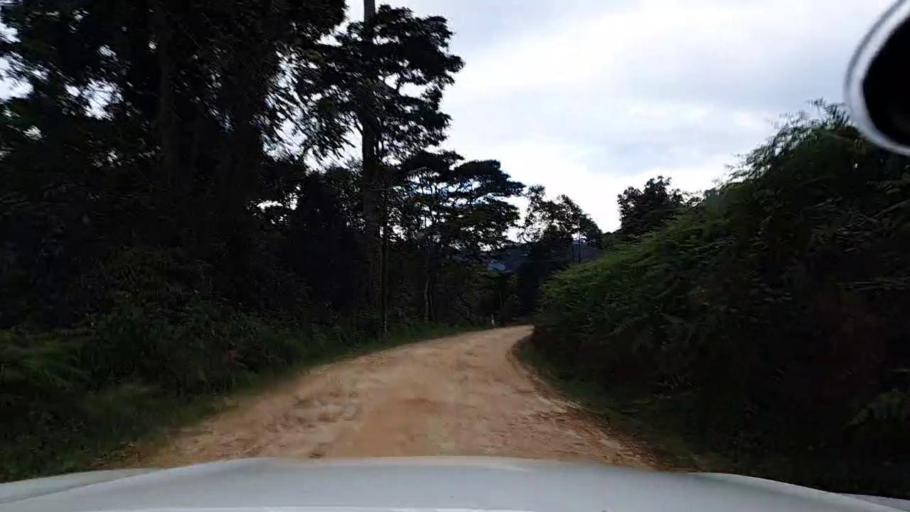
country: RW
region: Western Province
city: Cyangugu
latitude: -2.5692
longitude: 29.2287
